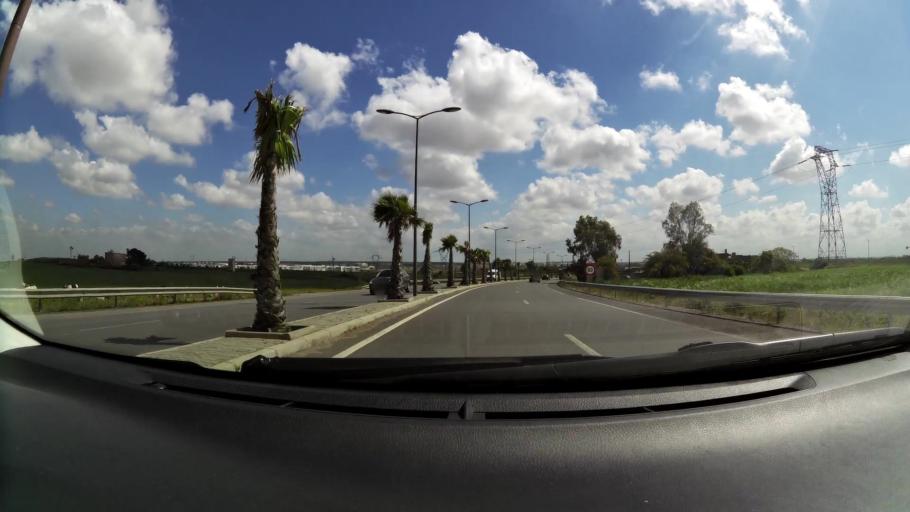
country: MA
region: Grand Casablanca
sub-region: Nouaceur
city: Bouskoura
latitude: 33.5023
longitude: -7.6083
